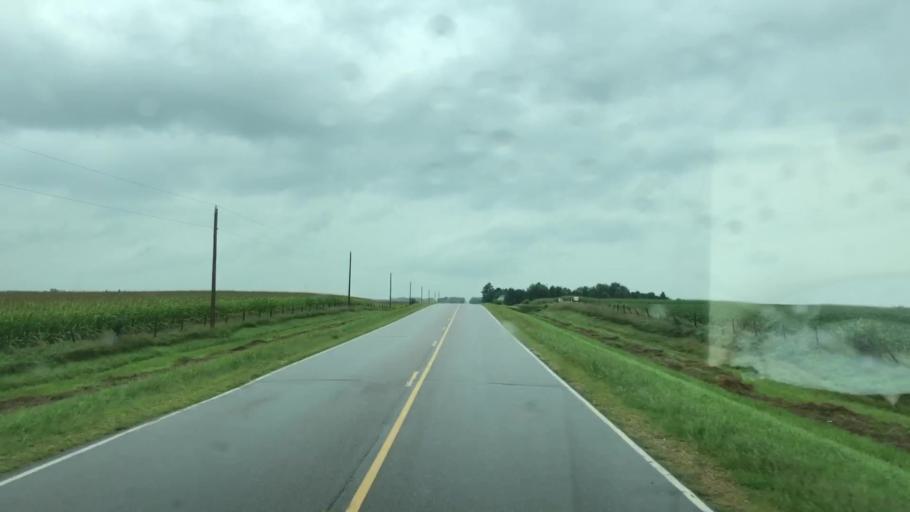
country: US
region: Iowa
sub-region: O'Brien County
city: Sanborn
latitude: 43.2545
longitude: -95.7235
